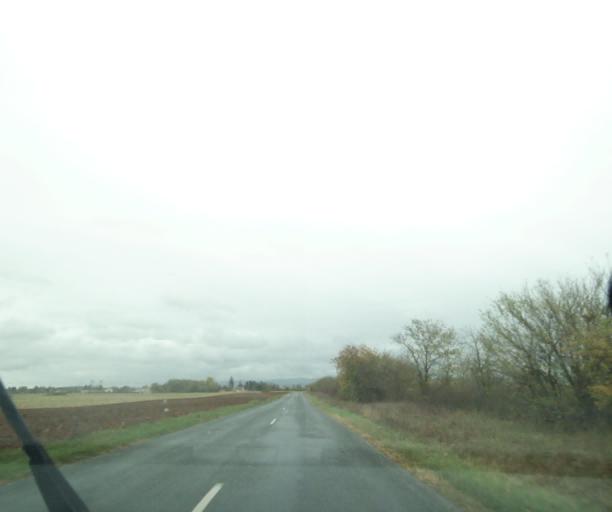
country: FR
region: Rhone-Alpes
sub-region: Departement de l'Ain
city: Loyettes
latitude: 45.7993
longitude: 5.2339
